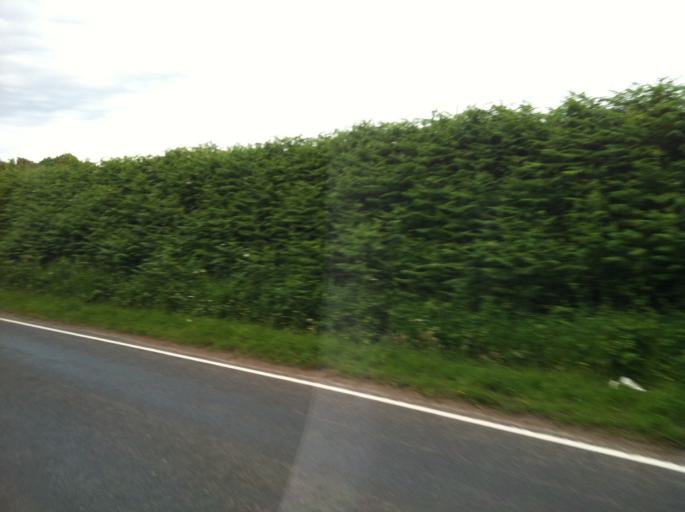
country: GB
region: Wales
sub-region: Bridgend county borough
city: Merthyr Mawr
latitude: 51.4822
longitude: -3.5934
